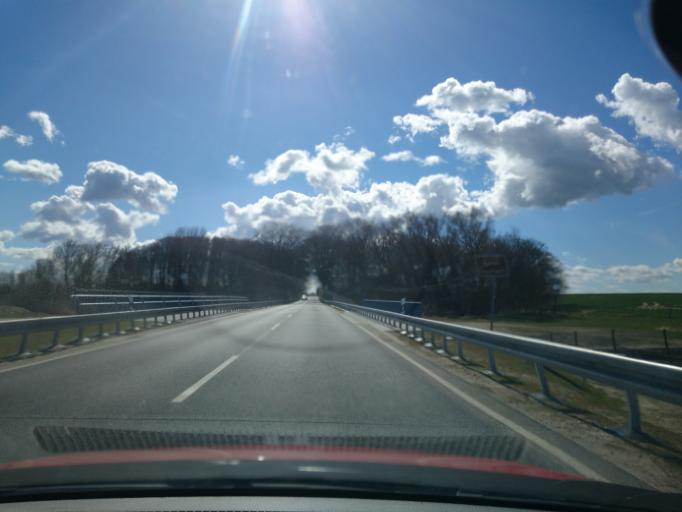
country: DE
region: Mecklenburg-Vorpommern
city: Barth
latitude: 54.3013
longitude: 12.7185
